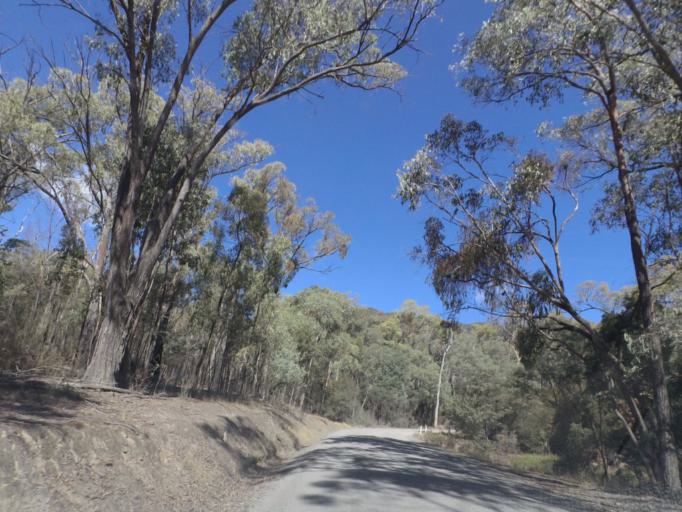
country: AU
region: Victoria
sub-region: Murrindindi
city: Alexandra
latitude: -37.3106
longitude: 145.8184
